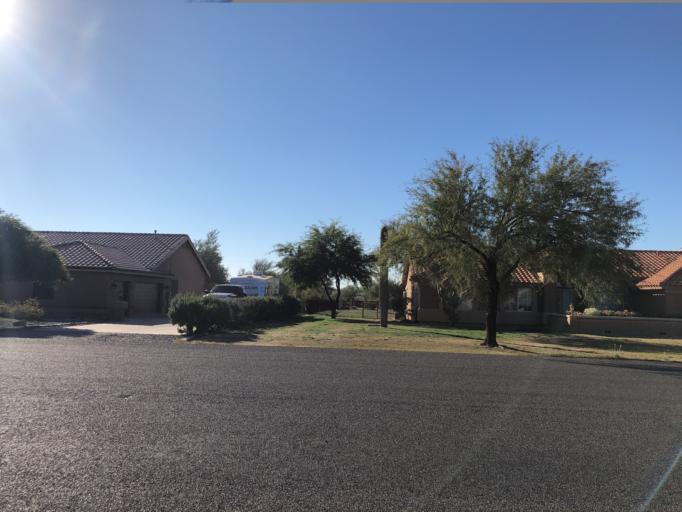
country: US
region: Arizona
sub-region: Maricopa County
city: Anthem
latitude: 33.8355
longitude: -112.0703
